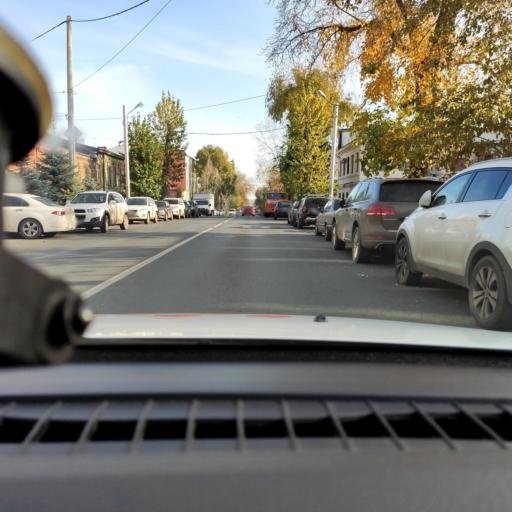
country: RU
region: Samara
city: Rozhdestveno
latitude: 53.1815
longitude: 50.0826
